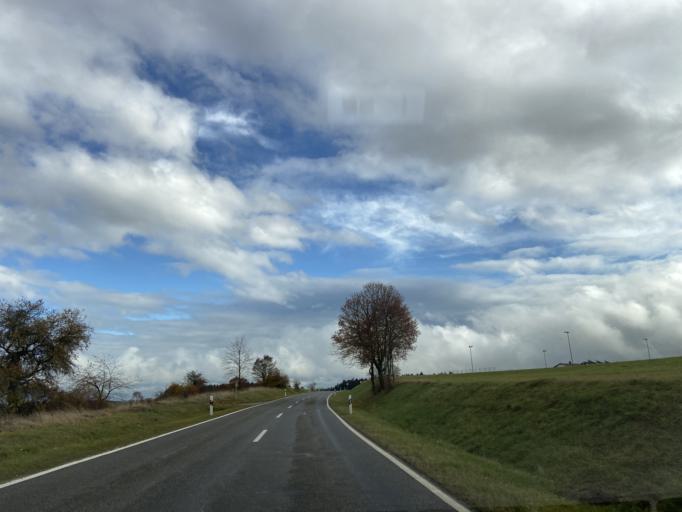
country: DE
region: Baden-Wuerttemberg
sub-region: Tuebingen Region
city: Leibertingen
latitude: 48.0548
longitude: 9.0625
